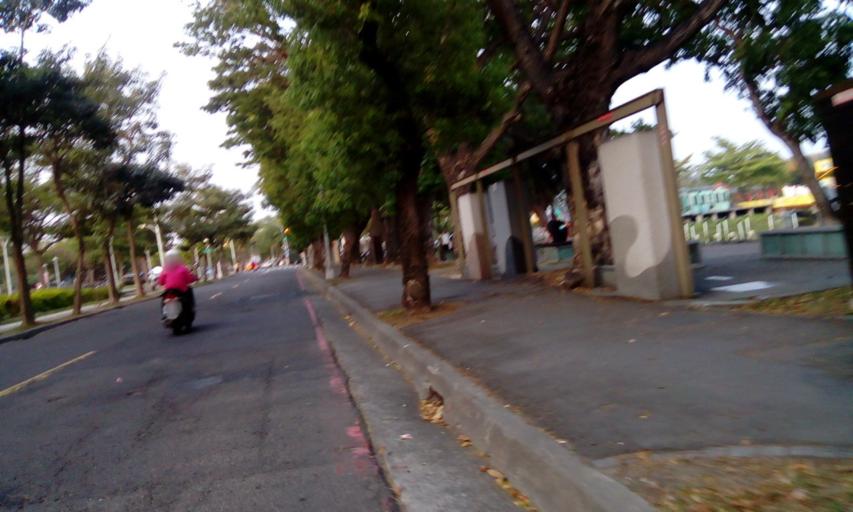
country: TW
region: Kaohsiung
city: Kaohsiung
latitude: 22.6870
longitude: 120.2969
